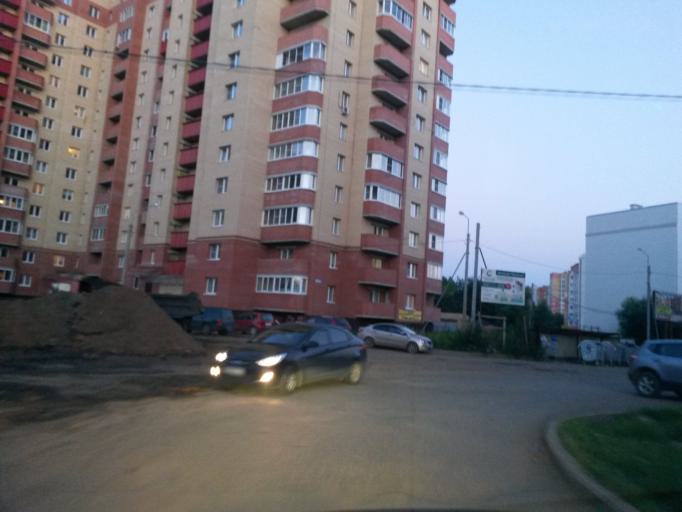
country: RU
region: Jaroslavl
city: Yaroslavl
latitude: 57.6963
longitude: 39.7822
